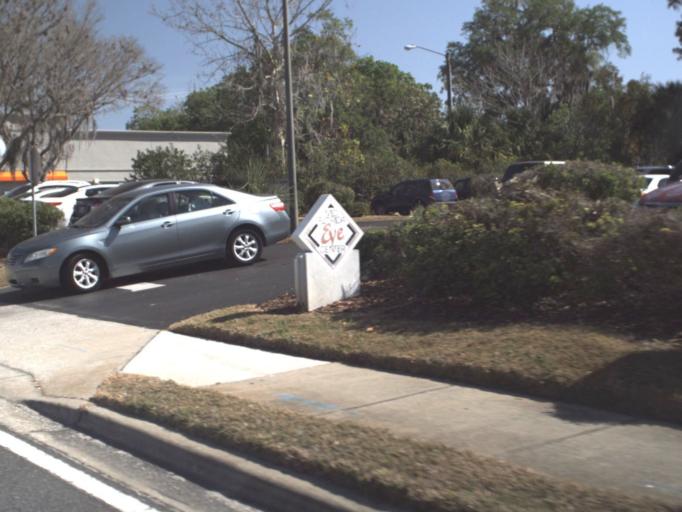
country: US
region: Florida
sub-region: Lake County
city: Leesburg
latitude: 28.8170
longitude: -81.8874
